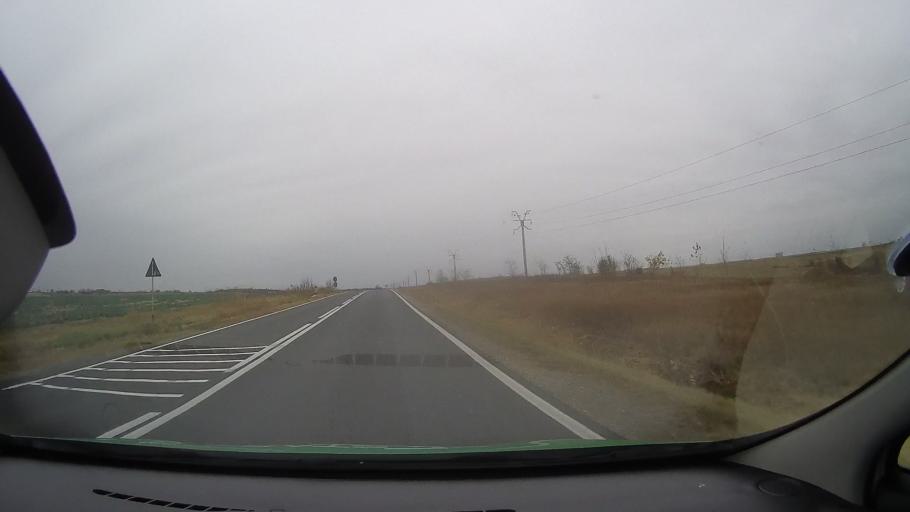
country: RO
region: Constanta
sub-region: Oras Harsova
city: Harsova
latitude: 44.6930
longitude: 27.9387
